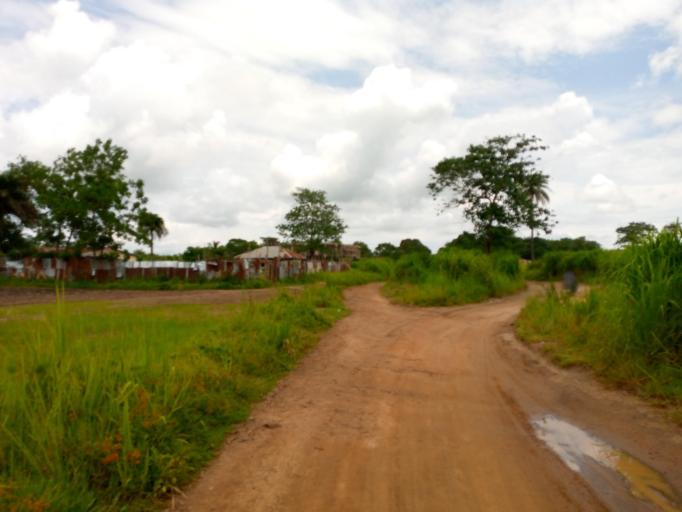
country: SL
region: Northern Province
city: Magburaka
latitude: 8.7099
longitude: -11.9634
